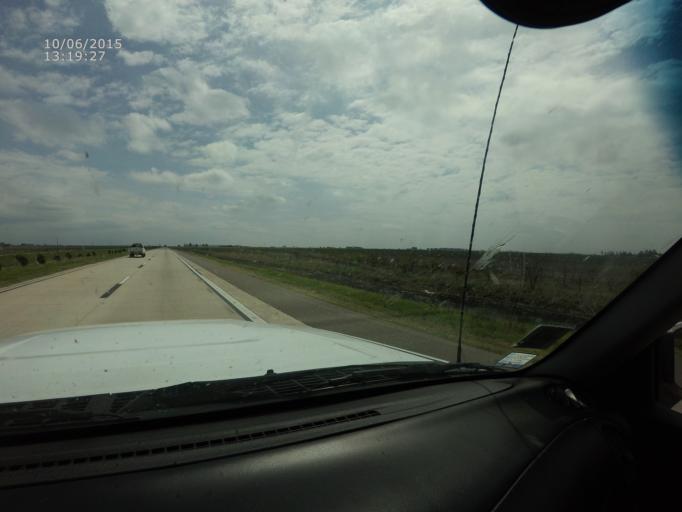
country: AR
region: Cordoba
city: Marcos Juarez
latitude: -32.6767
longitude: -62.0323
